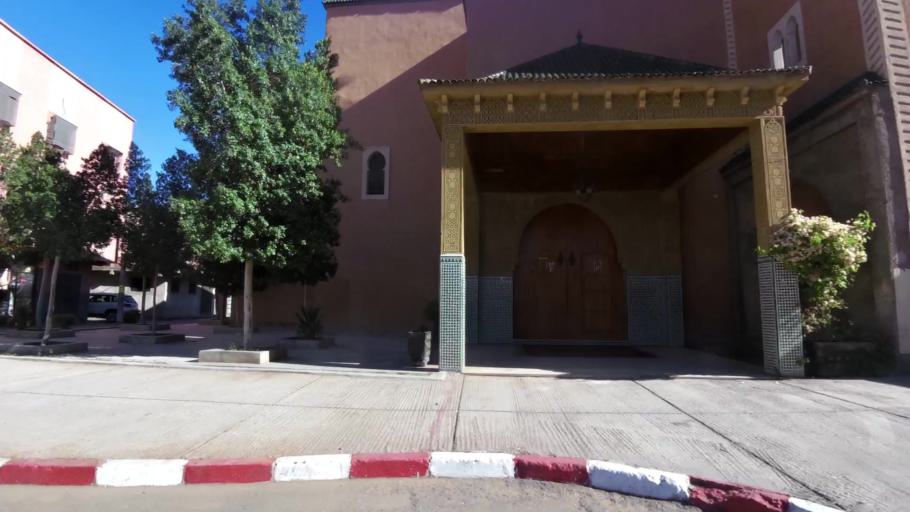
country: MA
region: Marrakech-Tensift-Al Haouz
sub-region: Marrakech
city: Marrakesh
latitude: 31.6008
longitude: -8.0339
